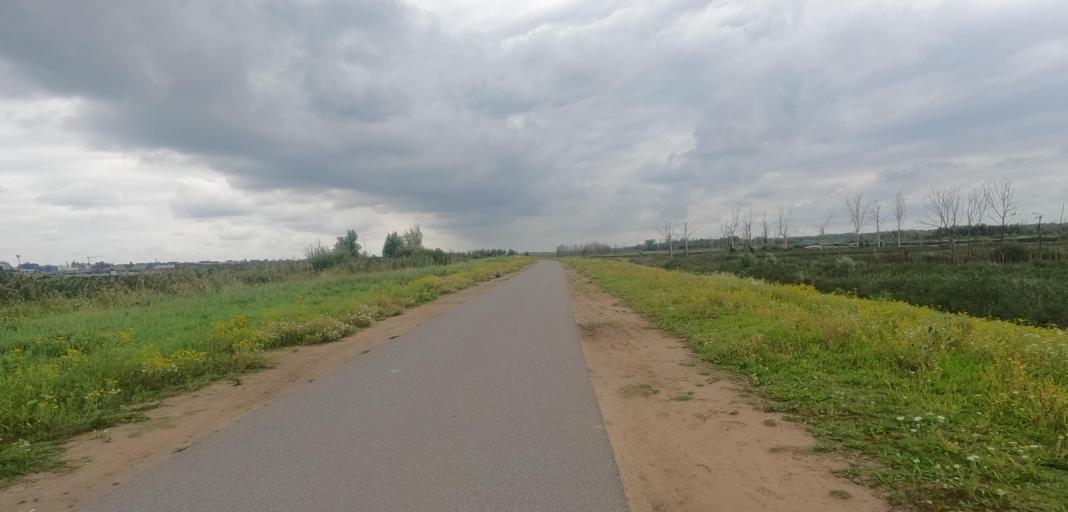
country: BE
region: Flanders
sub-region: Provincie Oost-Vlaanderen
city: Kruibeke
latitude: 51.1698
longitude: 4.3249
